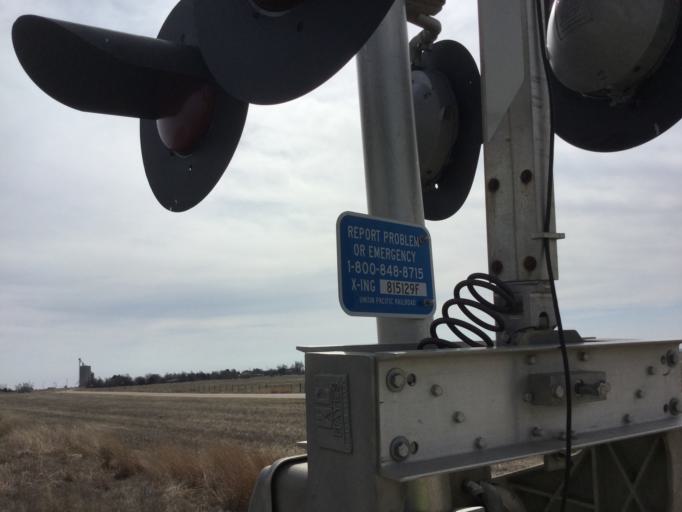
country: US
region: Kansas
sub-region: Trego County
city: WaKeeney
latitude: 38.9925
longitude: -99.7420
